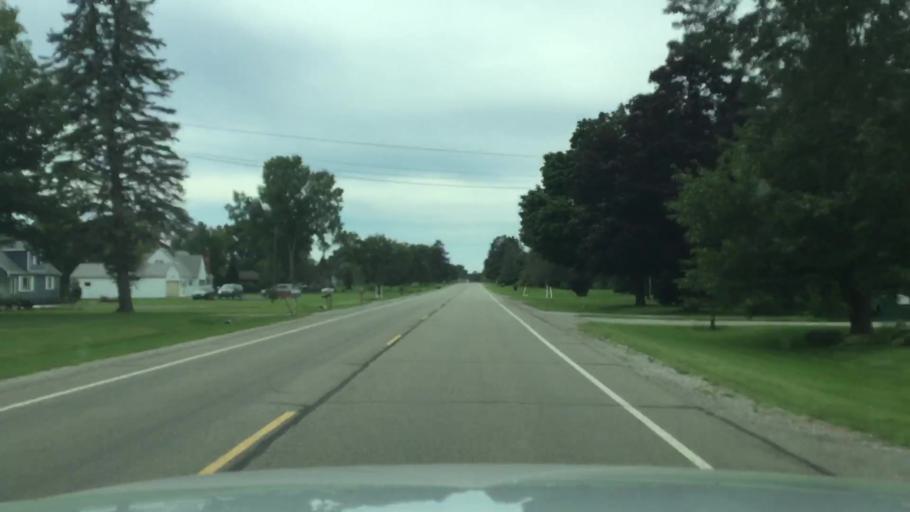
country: US
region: Michigan
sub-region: Shiawassee County
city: Durand
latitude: 42.9314
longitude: -83.9530
